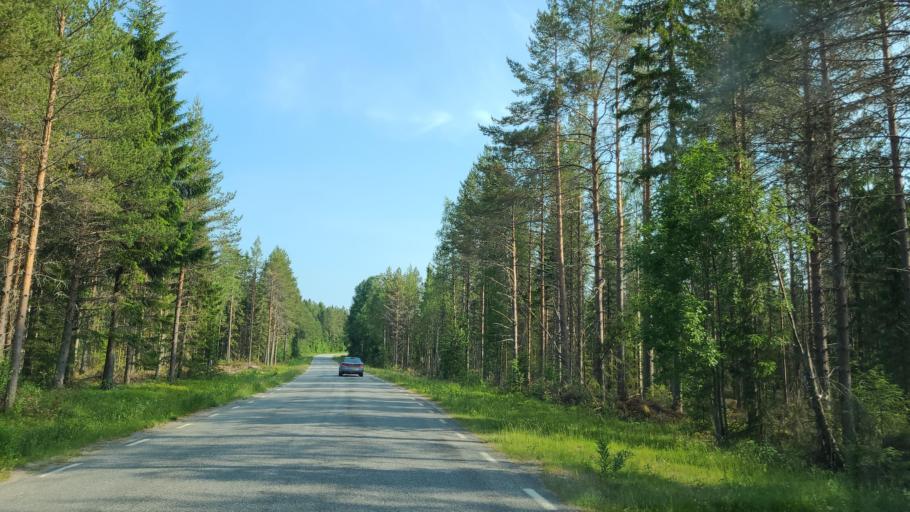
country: SE
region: Vaesterbotten
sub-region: Skelleftea Kommun
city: Burea
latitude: 64.3601
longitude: 21.3350
